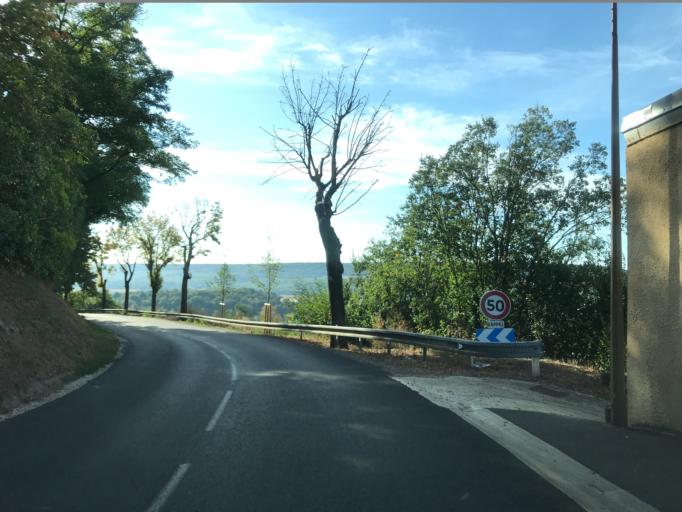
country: FR
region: Champagne-Ardenne
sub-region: Departement de la Marne
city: Chatillon-sur-Marne
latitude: 49.0985
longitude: 3.7574
